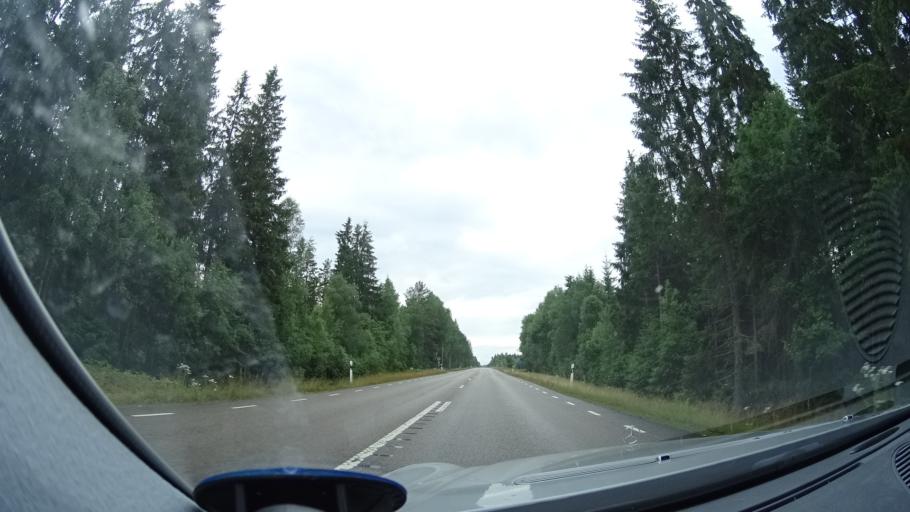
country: SE
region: Kronoberg
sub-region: Tingsryds Kommun
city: Tingsryd
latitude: 56.4592
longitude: 15.0014
